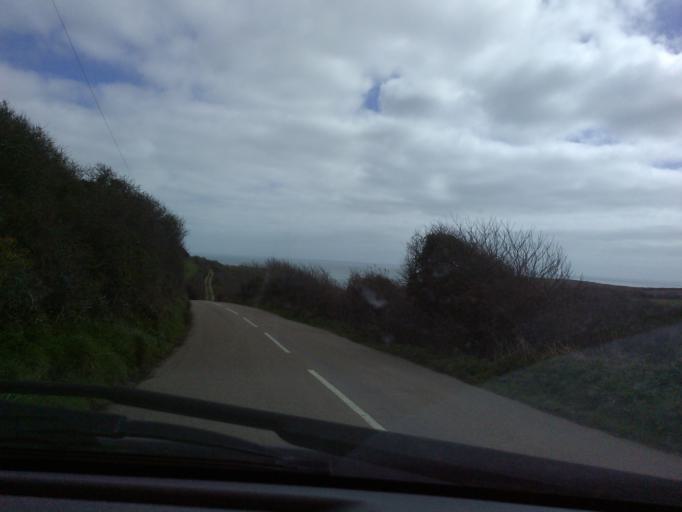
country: GB
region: England
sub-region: Cornwall
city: St. Buryan
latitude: 50.0541
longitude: -5.6375
